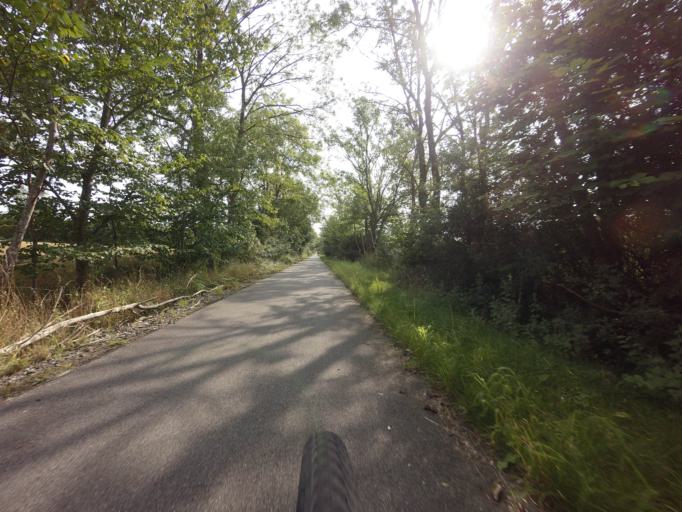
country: DK
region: Zealand
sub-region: Naestved Kommune
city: Fuglebjerg
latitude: 55.2612
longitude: 11.5765
